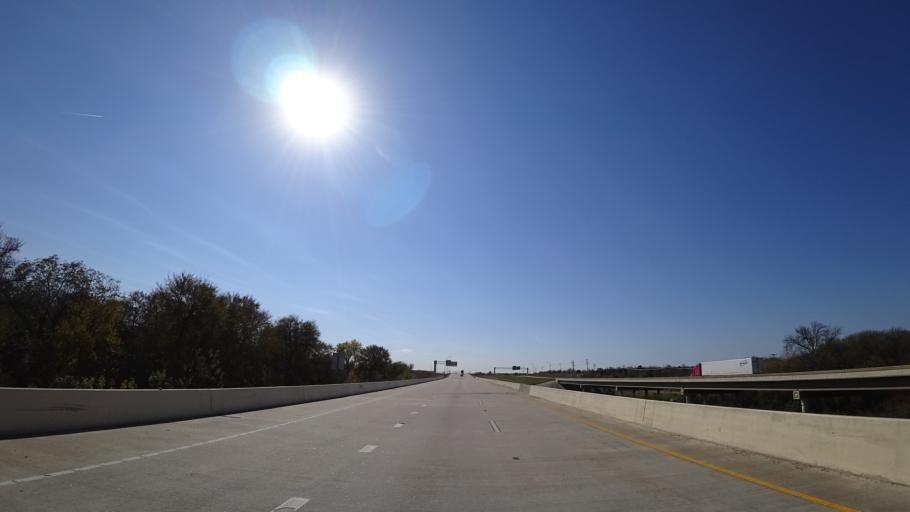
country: US
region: Texas
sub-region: Travis County
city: Manor
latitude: 30.3600
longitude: -97.5870
